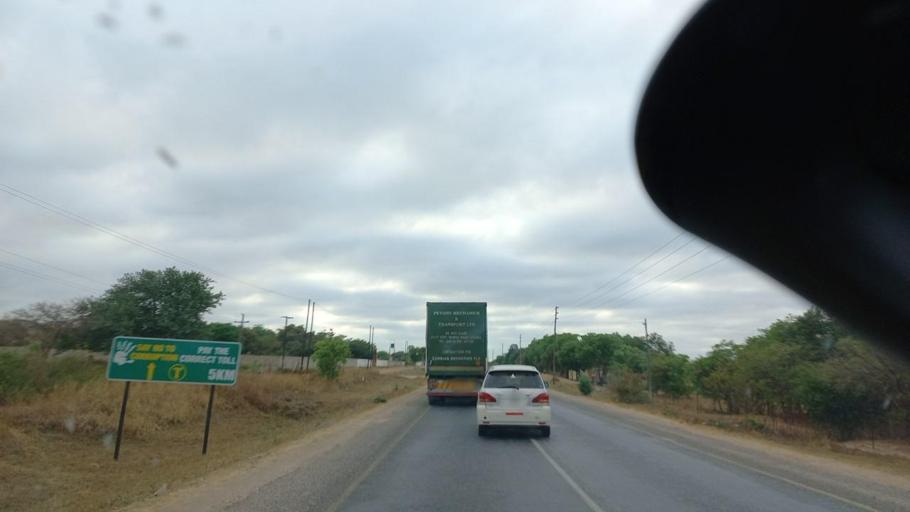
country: ZM
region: Lusaka
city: Chongwe
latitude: -15.3478
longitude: 28.5306
